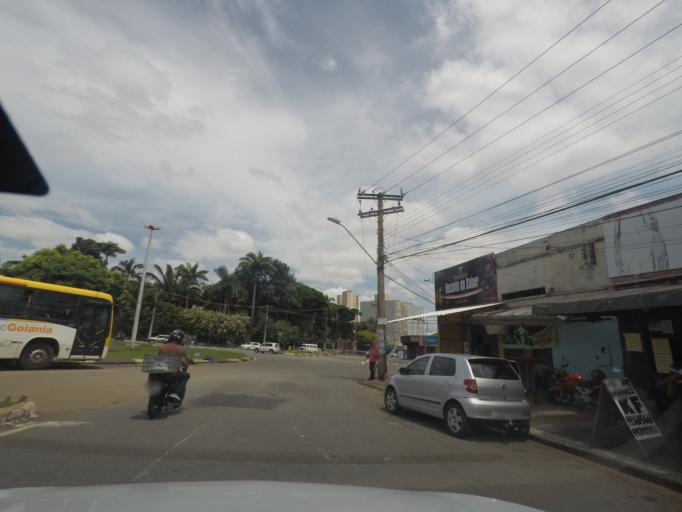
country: BR
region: Goias
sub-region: Goiania
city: Goiania
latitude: -16.6713
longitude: -49.2368
